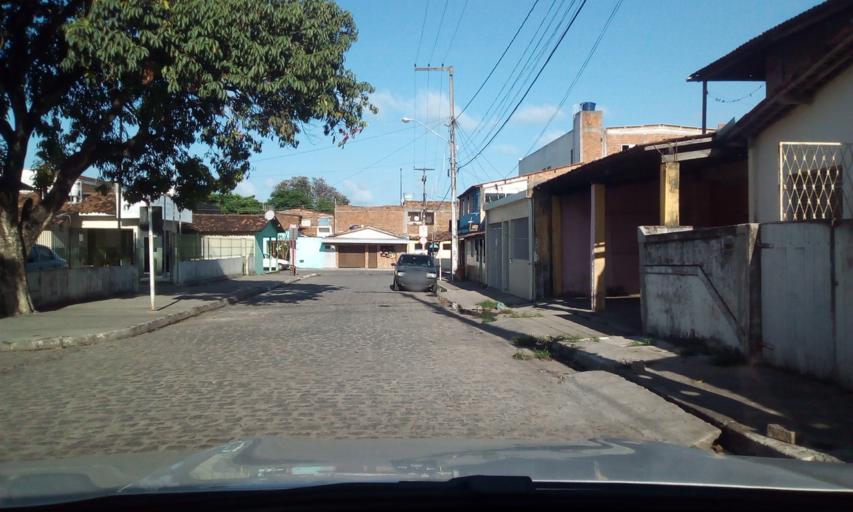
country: BR
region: Paraiba
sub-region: Joao Pessoa
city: Joao Pessoa
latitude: -7.0767
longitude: -34.8506
